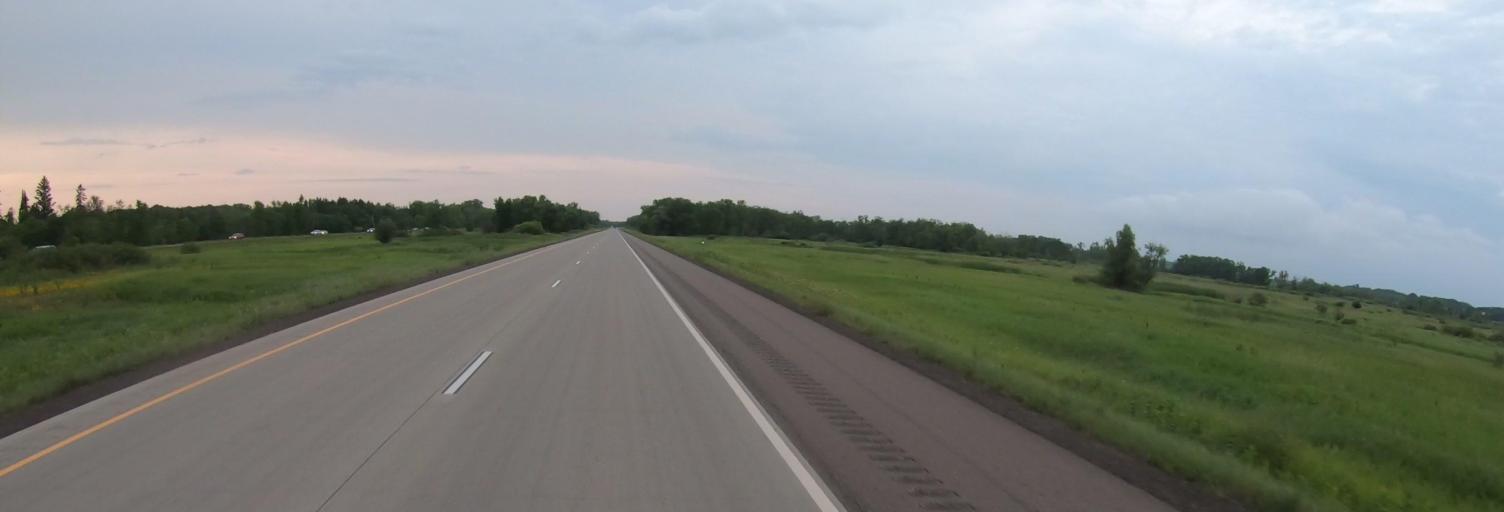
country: US
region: Minnesota
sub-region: Pine County
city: Hinckley
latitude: 45.9225
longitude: -92.9665
